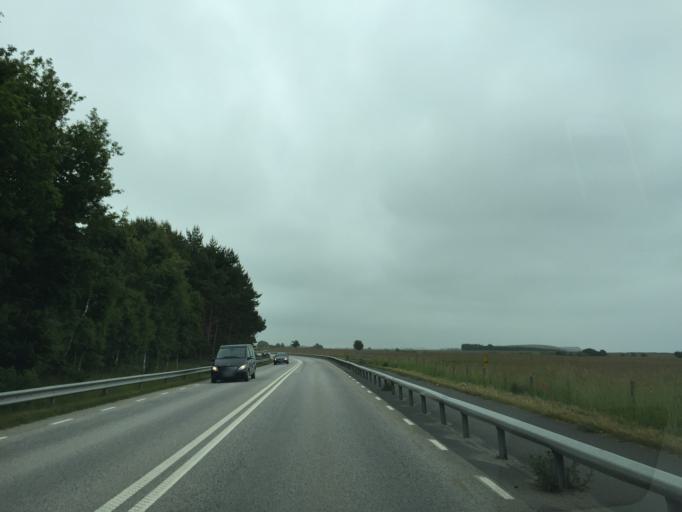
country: SE
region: Skane
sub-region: Ystads Kommun
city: Kopingebro
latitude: 55.4310
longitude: 13.9602
